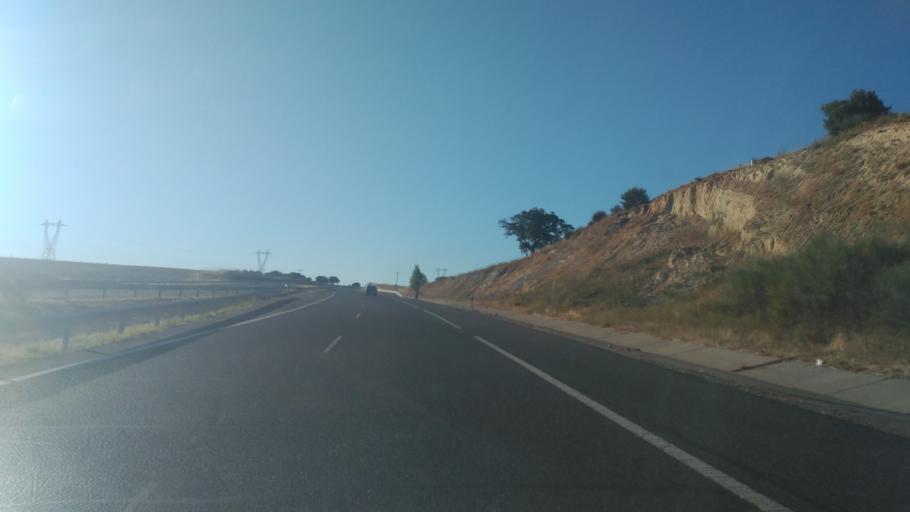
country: ES
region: Castille and Leon
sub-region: Provincia de Salamanca
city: Belena
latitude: 40.7184
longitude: -5.6263
